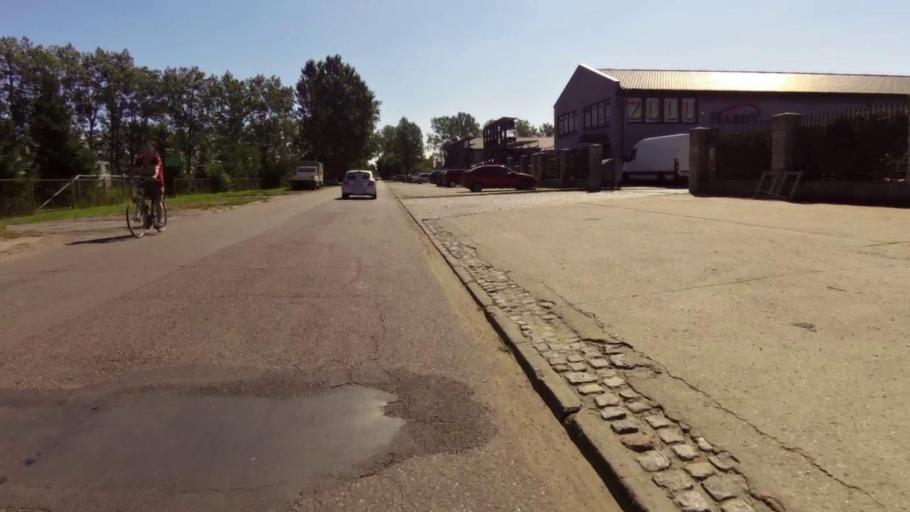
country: PL
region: West Pomeranian Voivodeship
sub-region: Powiat drawski
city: Zlocieniec
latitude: 53.5259
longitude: 16.0197
